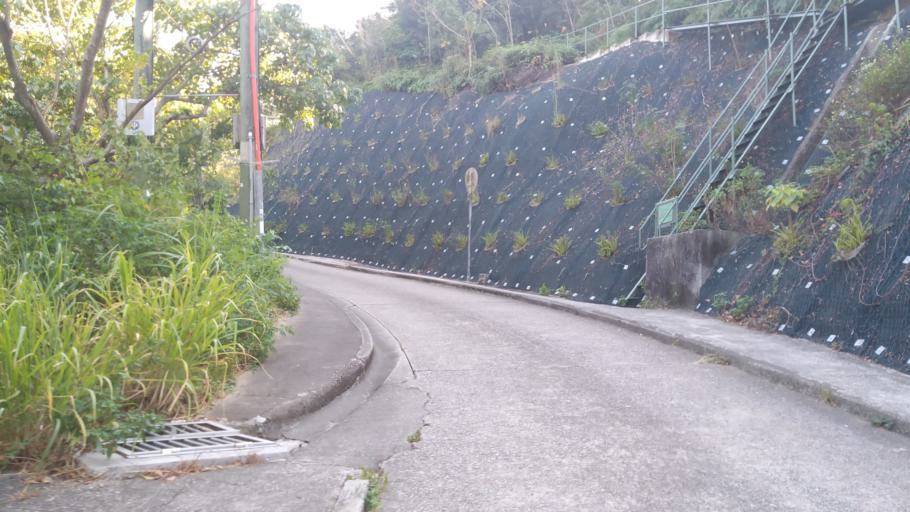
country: HK
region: Tuen Mun
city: Tuen Mun
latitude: 22.4078
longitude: 113.9849
